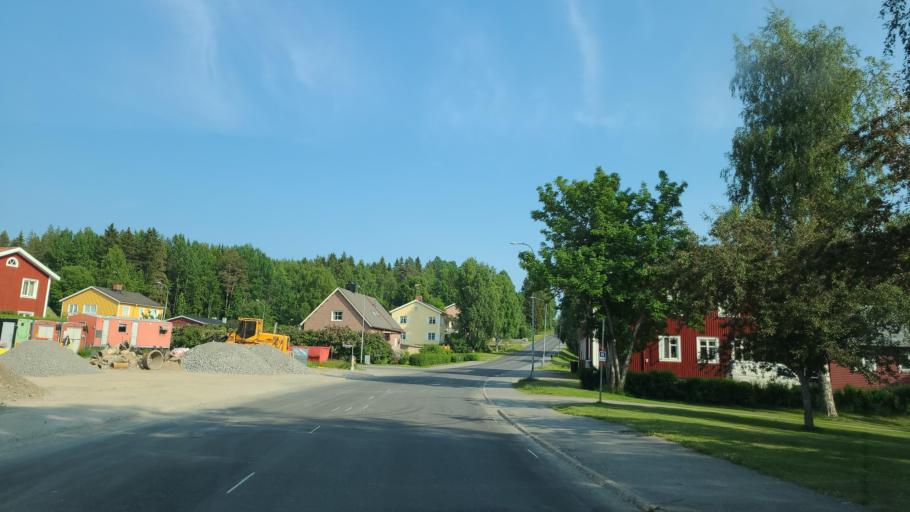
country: SE
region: Vaesterbotten
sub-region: Skelleftea Kommun
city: Burea
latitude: 64.3683
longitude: 21.3209
